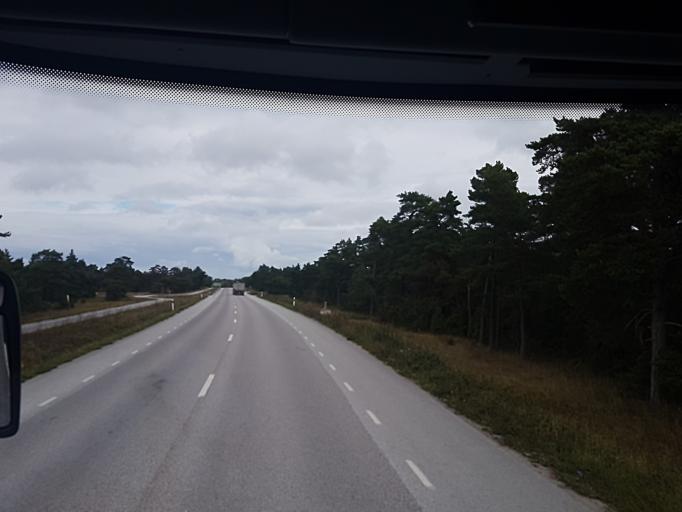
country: SE
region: Gotland
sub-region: Gotland
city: Vibble
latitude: 57.5629
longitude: 18.2045
